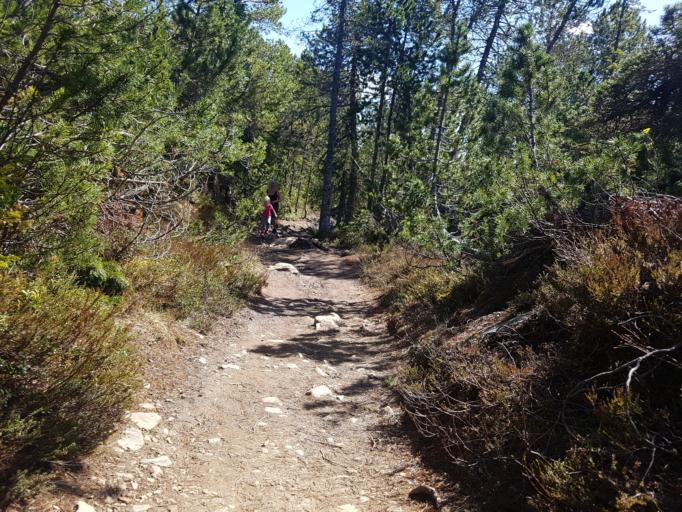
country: NO
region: Sor-Trondelag
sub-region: Trondheim
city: Trondheim
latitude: 63.4304
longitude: 10.3103
